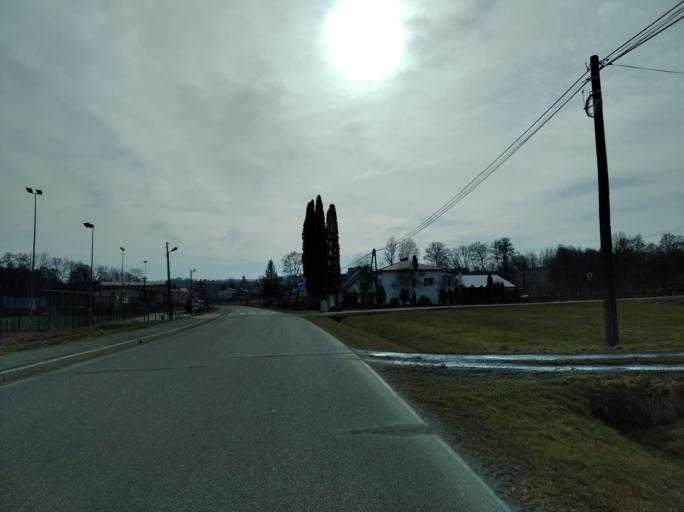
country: PL
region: Subcarpathian Voivodeship
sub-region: Powiat brzozowski
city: Orzechowka
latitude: 49.7332
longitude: 21.9436
